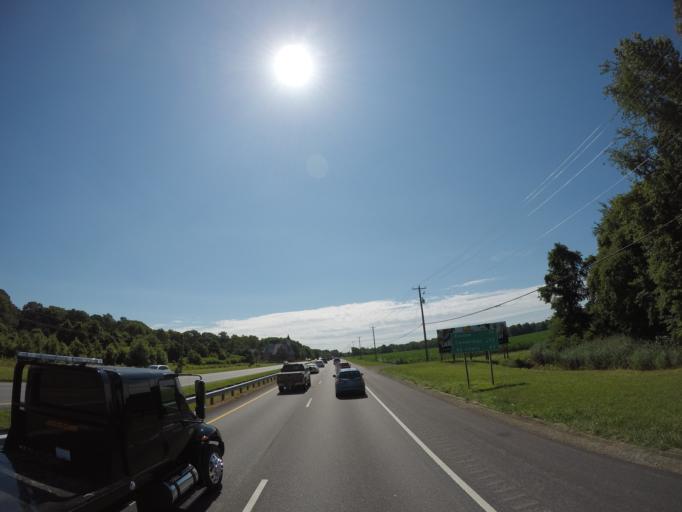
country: US
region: Maryland
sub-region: Queen Anne's County
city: Grasonville
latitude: 38.9782
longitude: -76.1359
